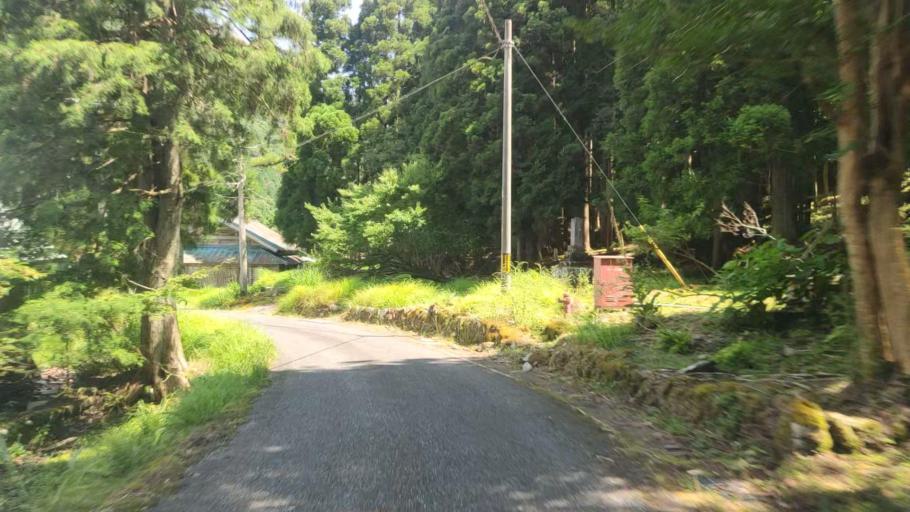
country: JP
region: Gifu
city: Godo
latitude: 35.7072
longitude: 136.5860
